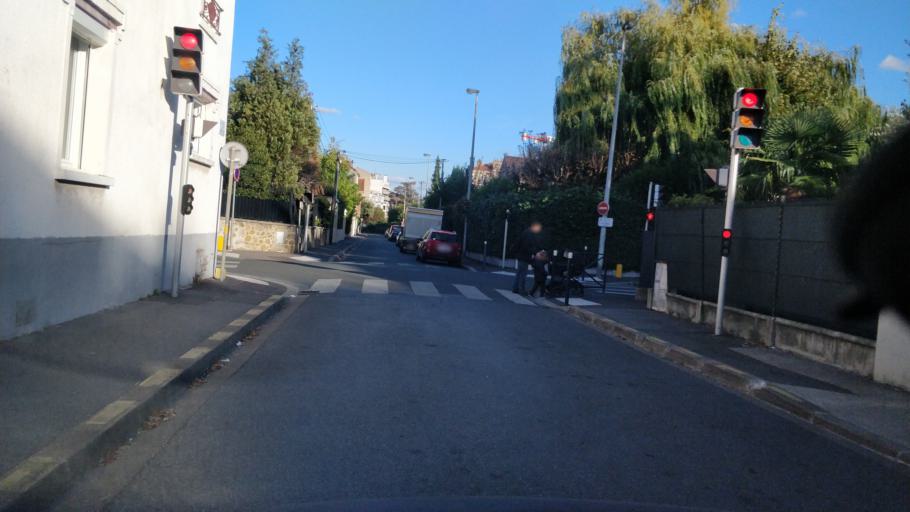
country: FR
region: Ile-de-France
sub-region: Departement de Seine-Saint-Denis
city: Villemomble
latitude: 48.8891
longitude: 2.5052
